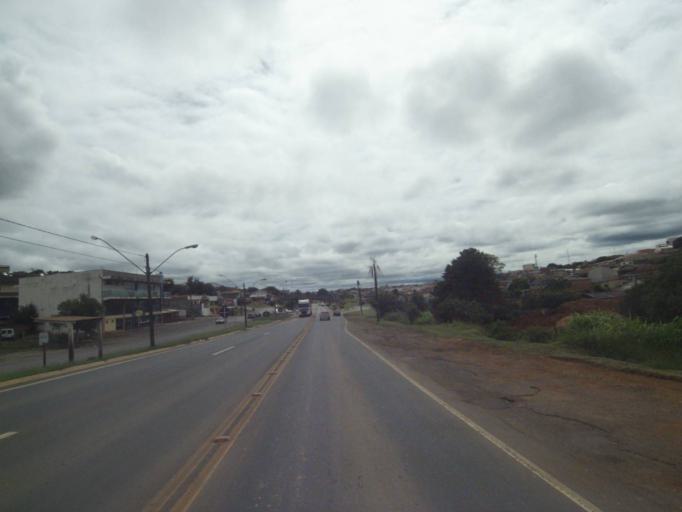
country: BR
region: Parana
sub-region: Telemaco Borba
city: Telemaco Borba
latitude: -24.3272
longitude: -50.6332
